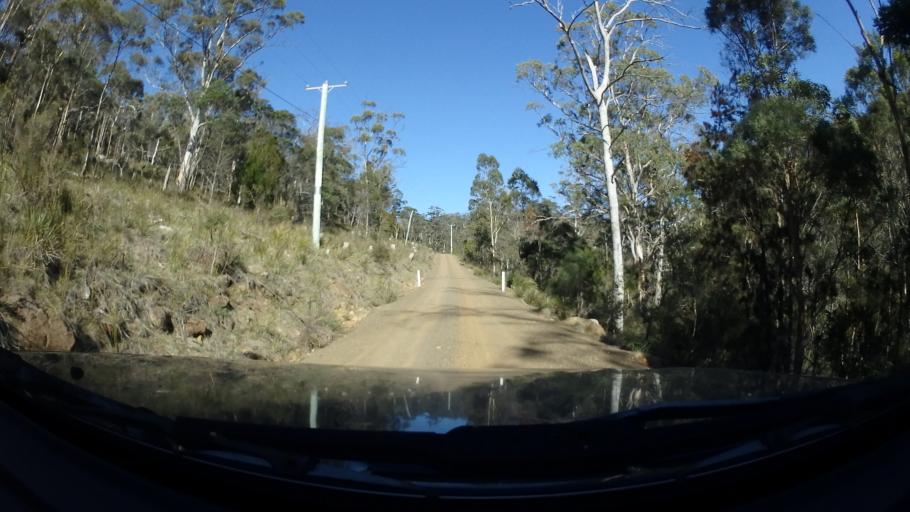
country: AU
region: Tasmania
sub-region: Sorell
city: Sorell
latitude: -42.5375
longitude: 147.8683
